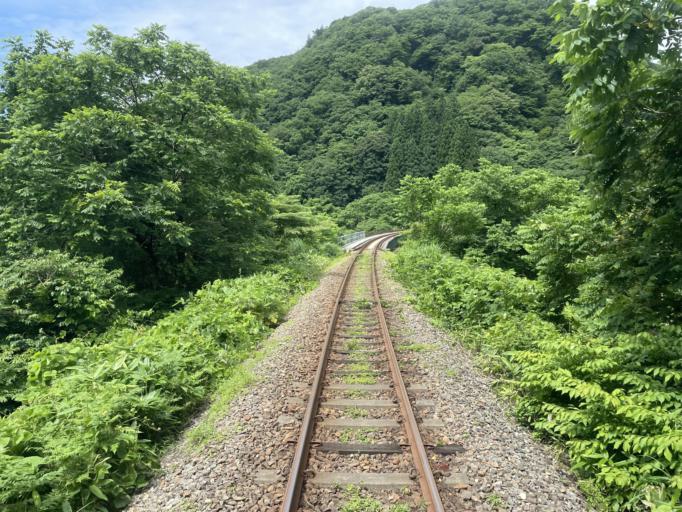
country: JP
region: Niigata
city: Murakami
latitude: 38.0681
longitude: 139.6168
